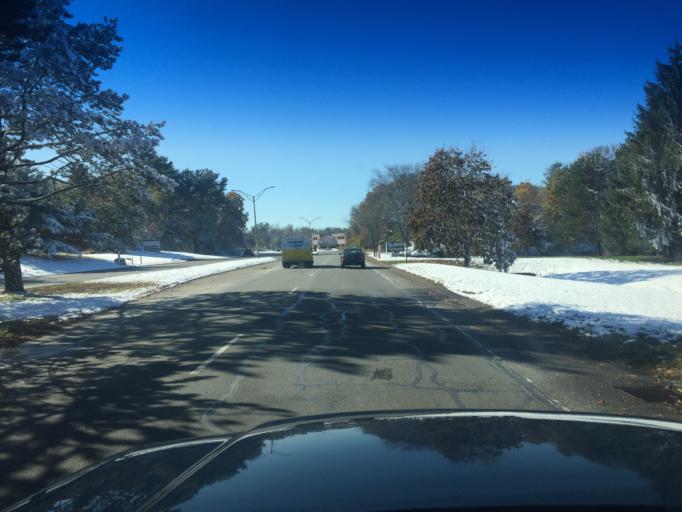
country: US
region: Massachusetts
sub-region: Bristol County
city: Norton
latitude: 41.9534
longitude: -71.1381
